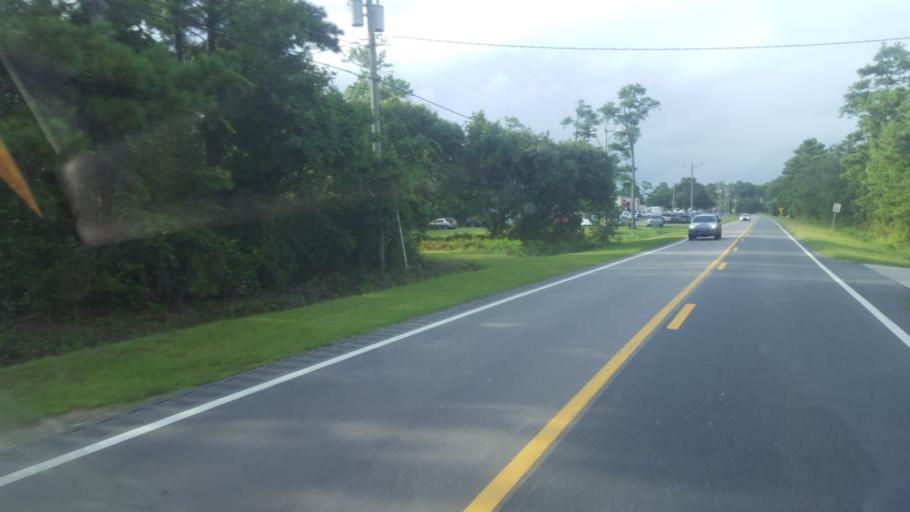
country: US
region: North Carolina
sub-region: Dare County
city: Manteo
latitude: 35.8847
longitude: -75.6588
